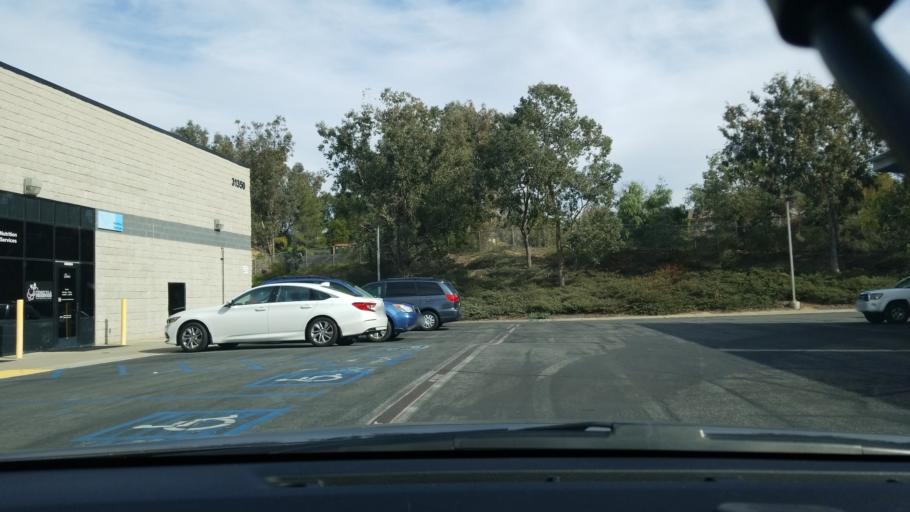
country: US
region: California
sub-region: Riverside County
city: Temecula
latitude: 33.5057
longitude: -117.1135
